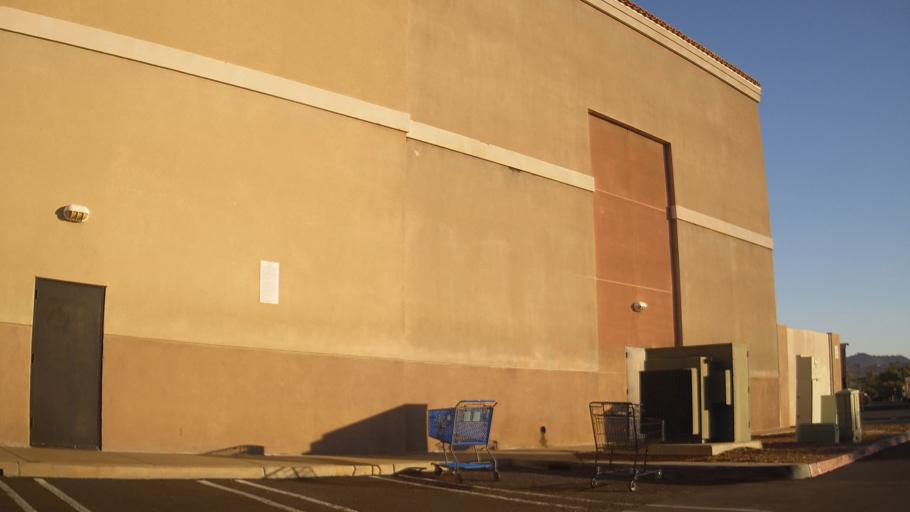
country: US
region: California
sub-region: San Diego County
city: Rancho San Diego
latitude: 32.7384
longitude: -116.9394
